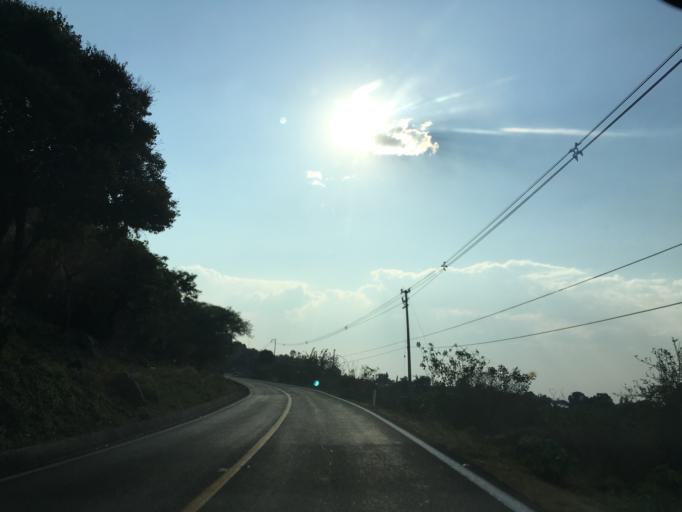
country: MX
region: Michoacan
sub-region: Indaparapeo
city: Colonia de Guadalupe
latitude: 19.8066
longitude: -100.8729
